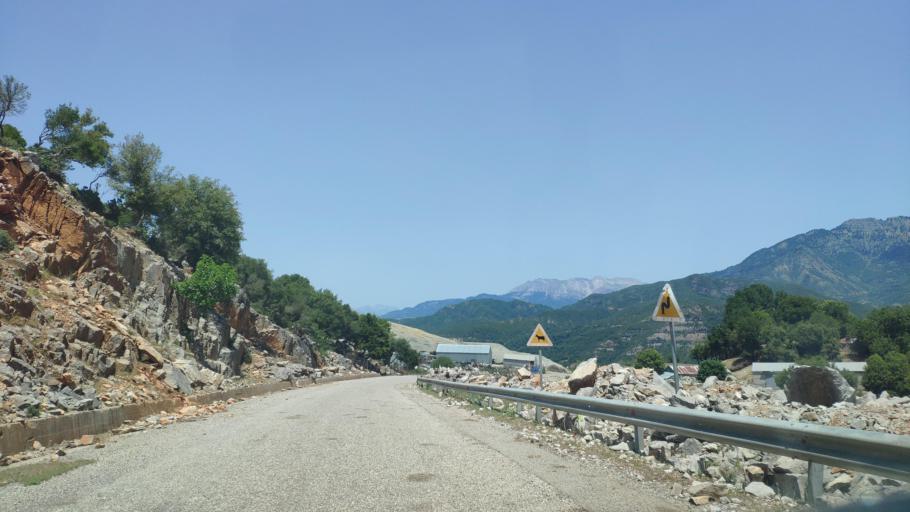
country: GR
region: Thessaly
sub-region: Nomos Kardhitsas
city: Anthiro
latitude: 39.1520
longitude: 21.3856
